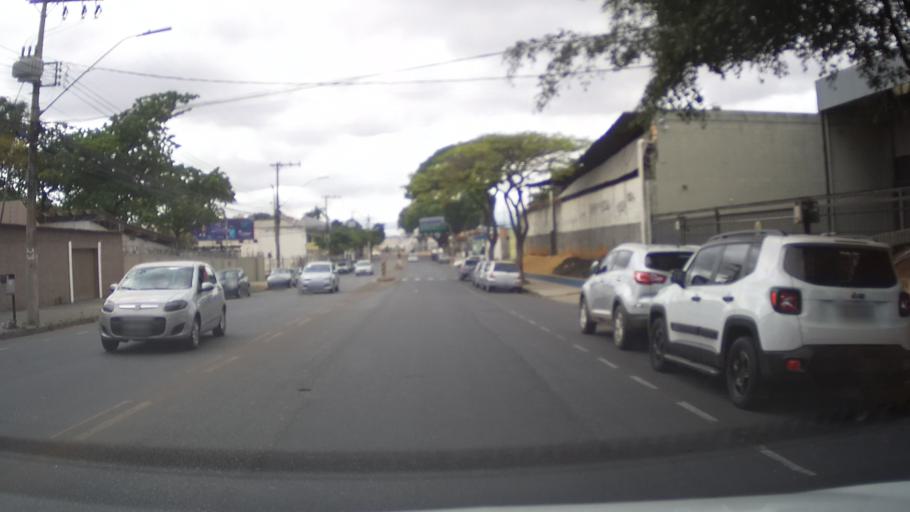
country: BR
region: Minas Gerais
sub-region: Belo Horizonte
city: Belo Horizonte
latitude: -19.8441
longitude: -43.9579
